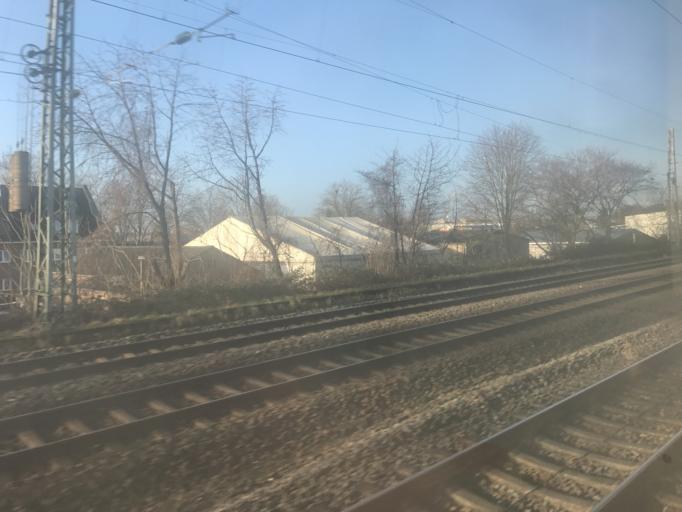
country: DE
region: North Rhine-Westphalia
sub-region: Regierungsbezirk Dusseldorf
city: Hilden
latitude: 51.1692
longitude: 6.8723
